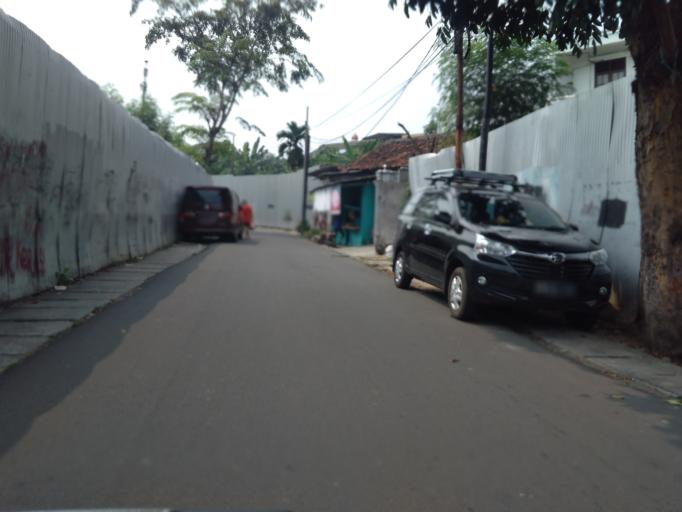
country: ID
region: Jakarta Raya
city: Jakarta
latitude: -6.2572
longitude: 106.7920
